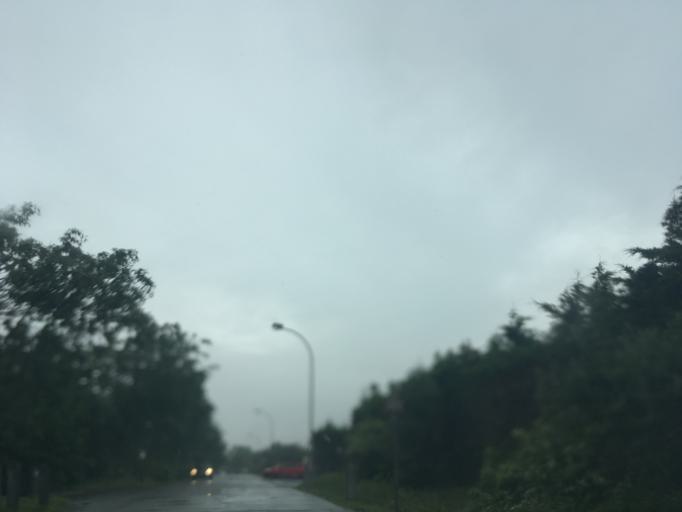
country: FR
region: Poitou-Charentes
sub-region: Departement de la Charente
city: Saint-Brice
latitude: 45.6779
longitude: -0.3068
